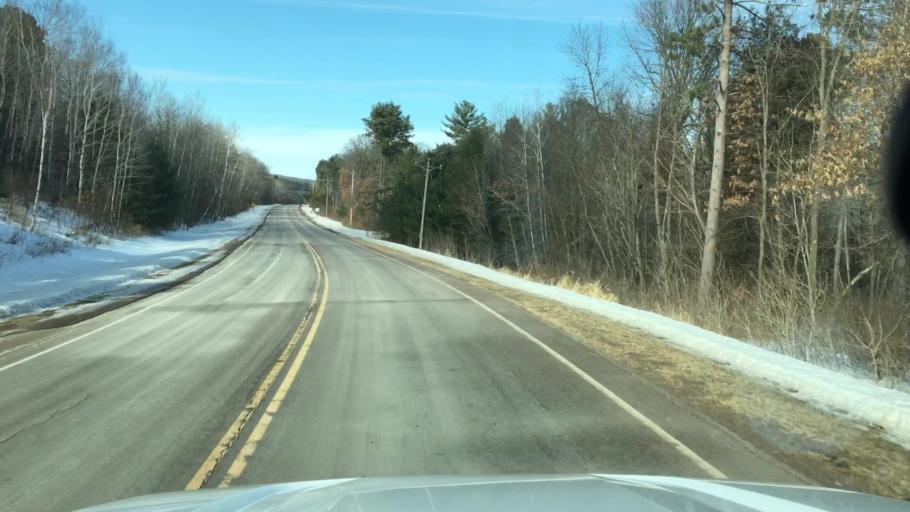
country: US
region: Wisconsin
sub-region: Polk County
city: Saint Croix Falls
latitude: 45.4586
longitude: -92.6751
